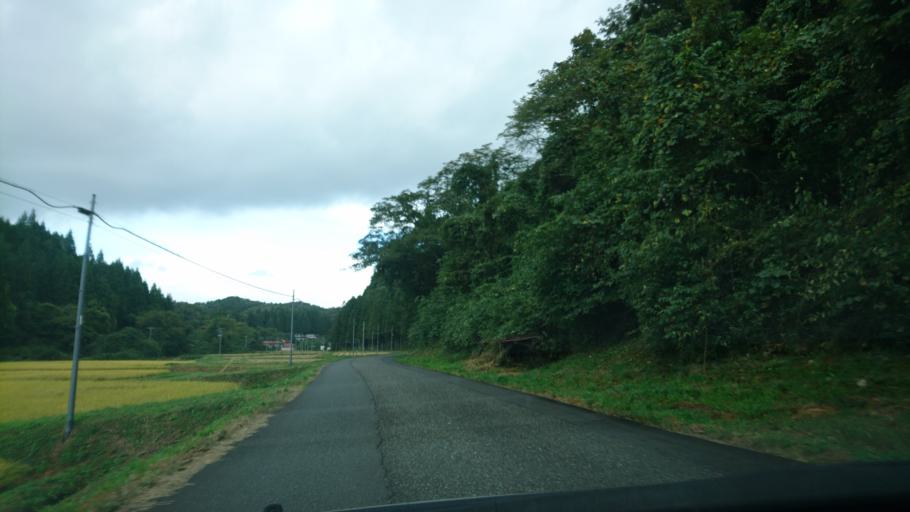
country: JP
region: Iwate
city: Ichinoseki
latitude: 38.8994
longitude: 141.0858
